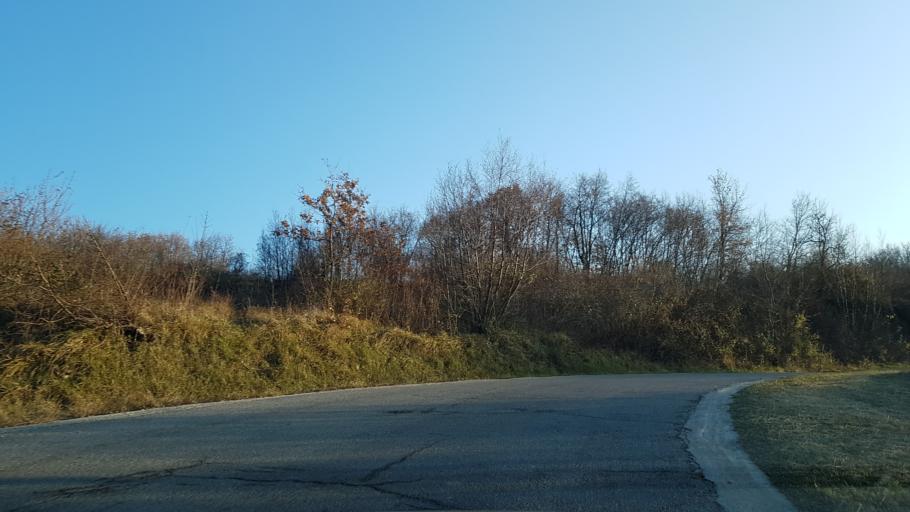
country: SI
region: Koper-Capodistria
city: Sv. Anton
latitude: 45.4908
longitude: 13.7988
